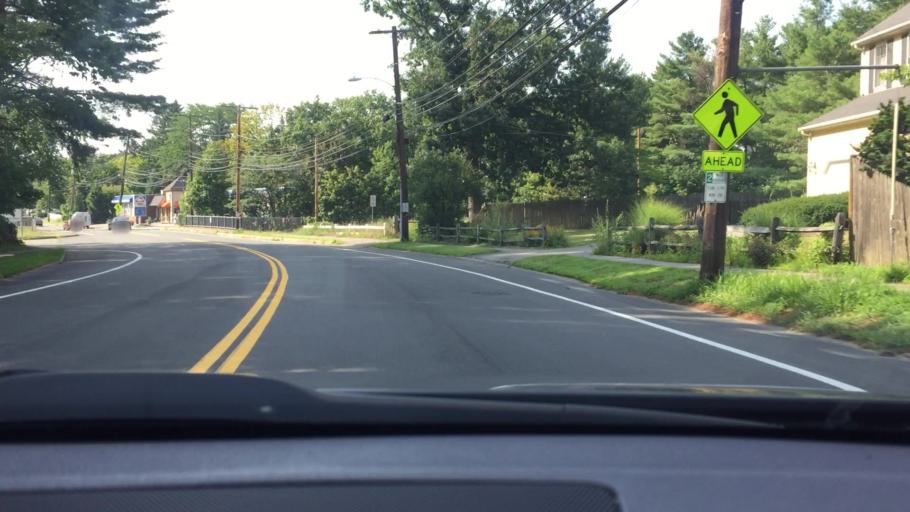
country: US
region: Massachusetts
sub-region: Norfolk County
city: Needham
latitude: 42.2752
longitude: -71.2140
